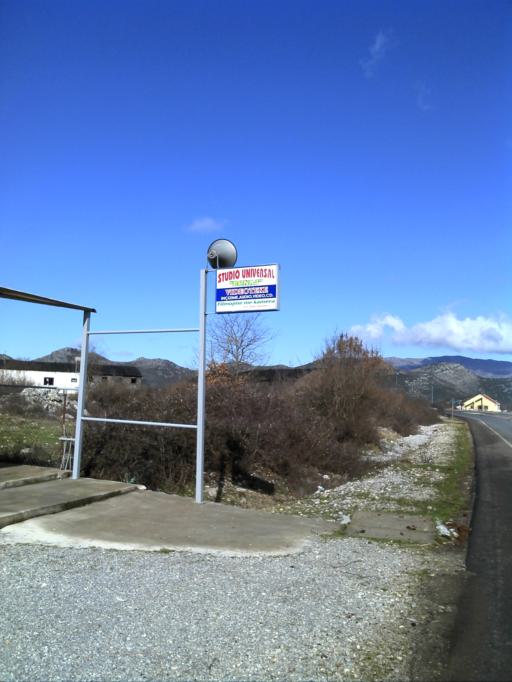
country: AL
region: Shkoder
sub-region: Rrethi i Malesia e Madhe
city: Koplik
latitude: 42.2865
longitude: 19.4403
